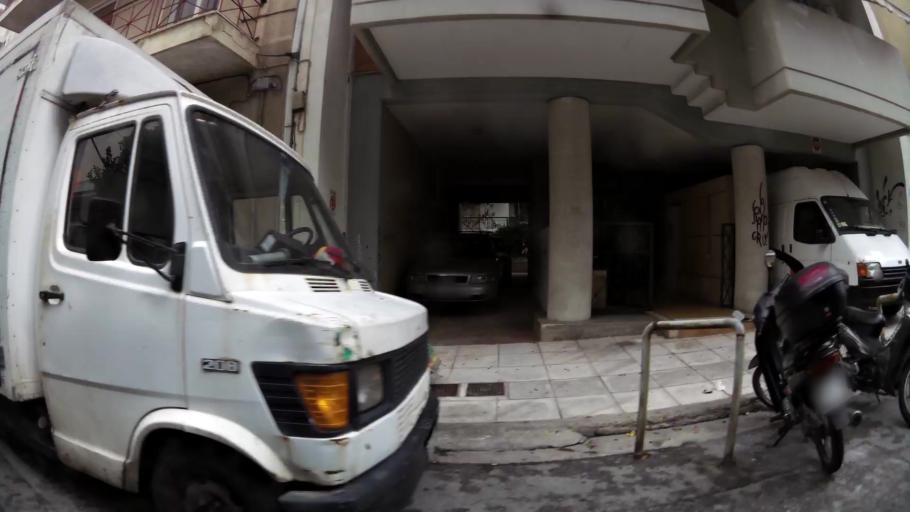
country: GR
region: Attica
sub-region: Nomarchia Athinas
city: Vyronas
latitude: 37.9648
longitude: 23.7523
